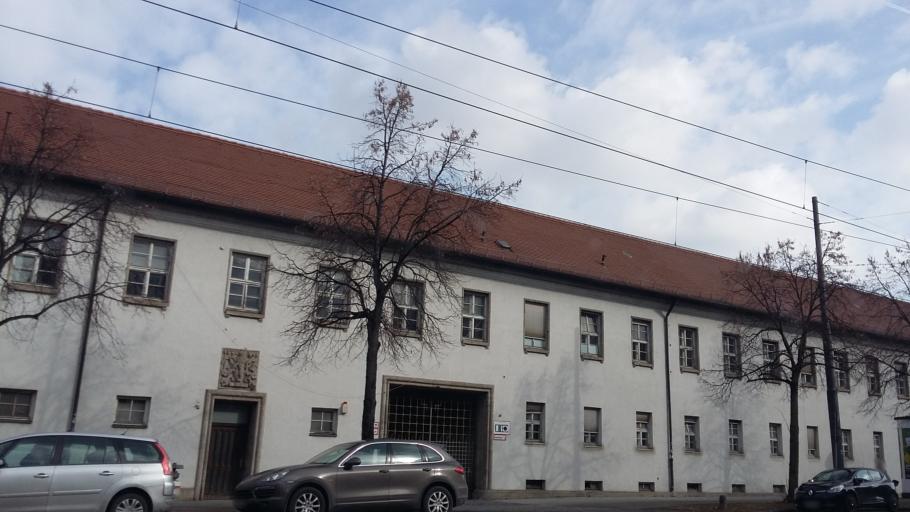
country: DE
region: Bavaria
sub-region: Upper Bavaria
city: Munich
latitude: 48.1438
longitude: 11.5471
